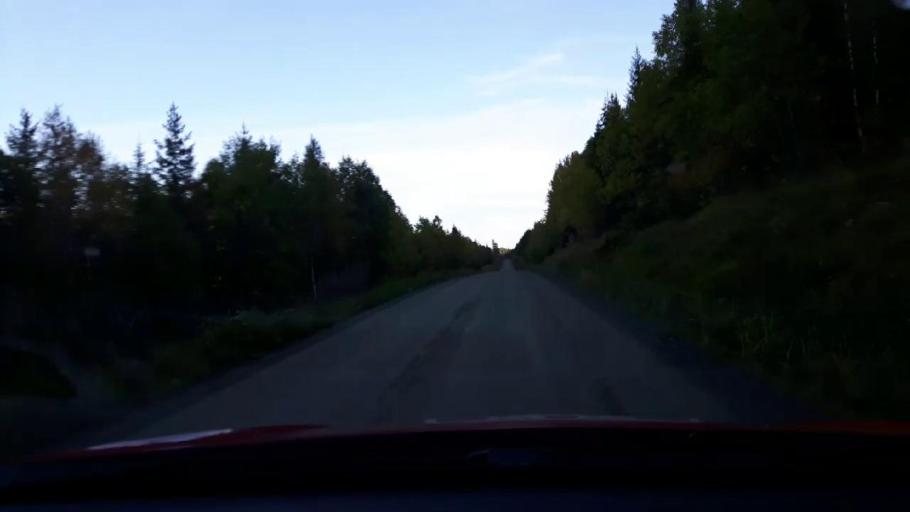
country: SE
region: Jaemtland
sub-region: OEstersunds Kommun
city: Brunflo
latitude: 62.9388
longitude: 14.9912
